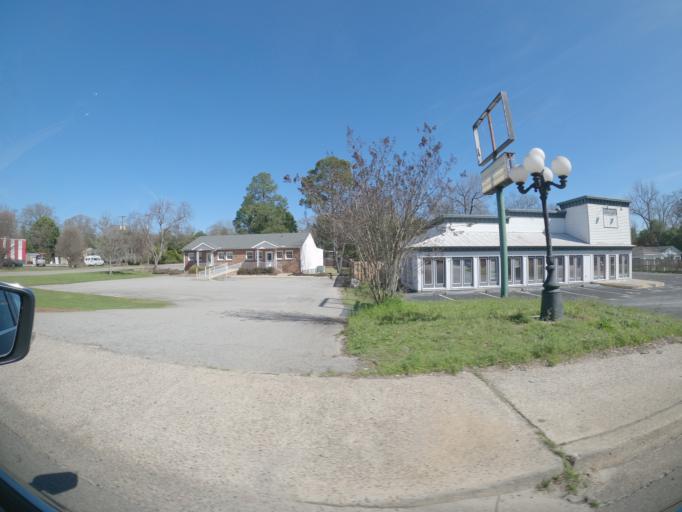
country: US
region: South Carolina
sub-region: Aiken County
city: North Augusta
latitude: 33.4935
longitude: -81.9559
